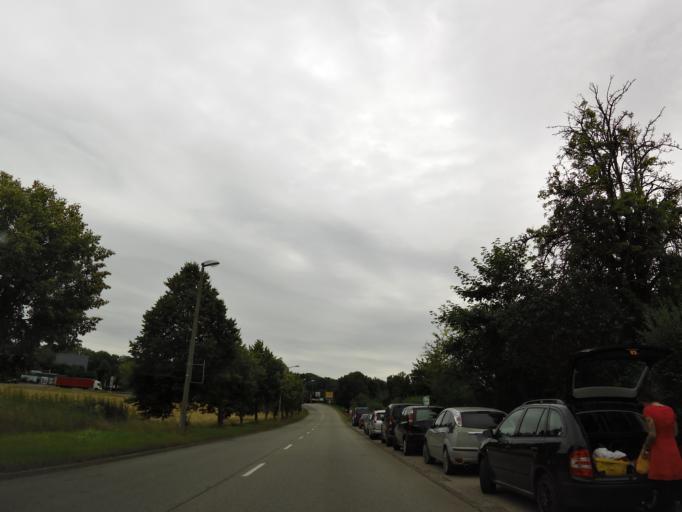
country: DE
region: Thuringia
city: Bad Langensalza
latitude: 51.1154
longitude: 10.6580
